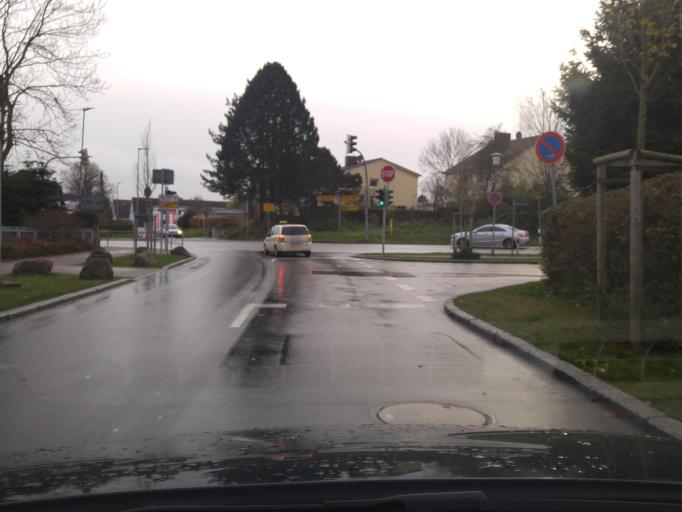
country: DE
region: Schleswig-Holstein
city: Timmendorfer Strand
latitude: 53.9938
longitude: 10.7692
